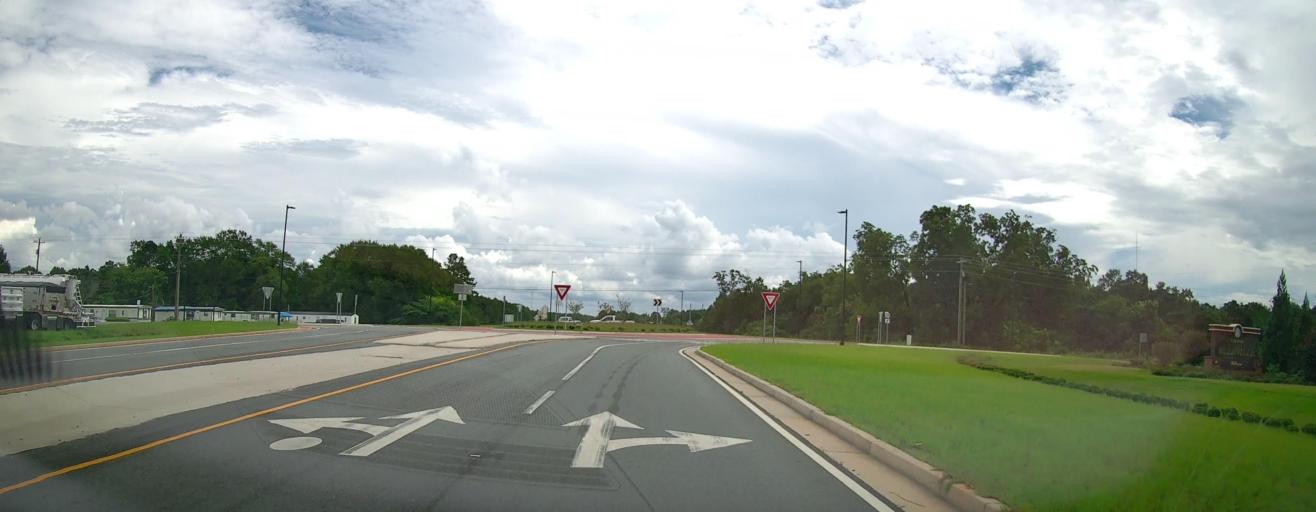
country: US
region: Georgia
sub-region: Schley County
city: Ellaville
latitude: 32.2405
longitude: -84.2963
